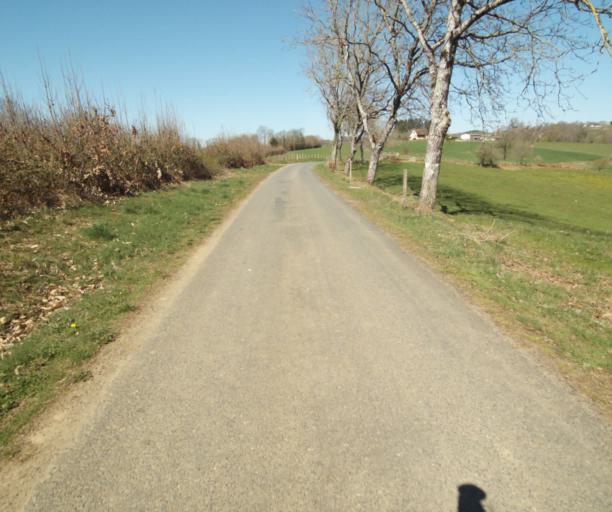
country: FR
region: Limousin
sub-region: Departement de la Correze
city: Saint-Clement
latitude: 45.3306
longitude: 1.7096
